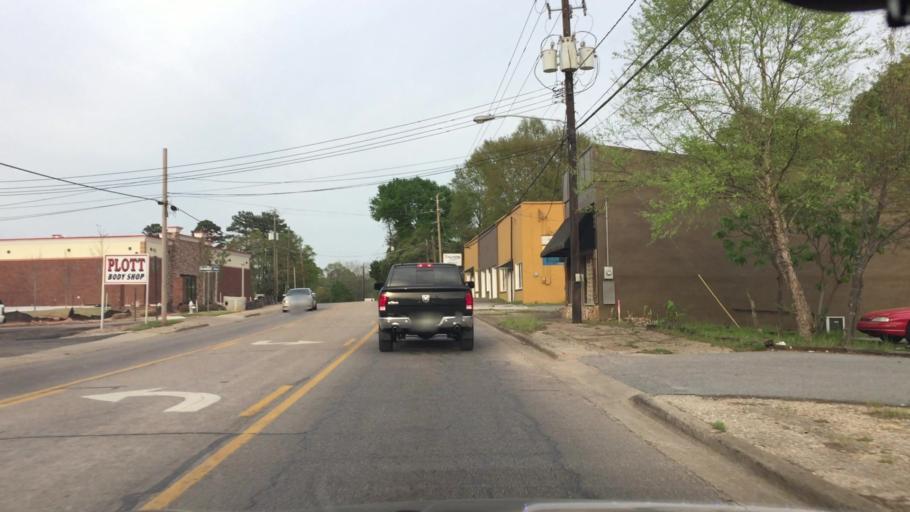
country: US
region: Alabama
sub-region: Lee County
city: Auburn
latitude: 32.6134
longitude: -85.4727
